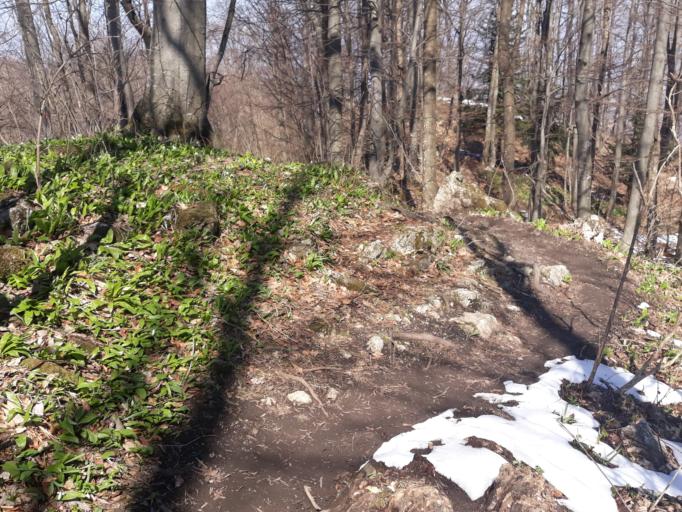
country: HR
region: Varazdinska
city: Ivanec
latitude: 46.1813
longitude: 16.1133
